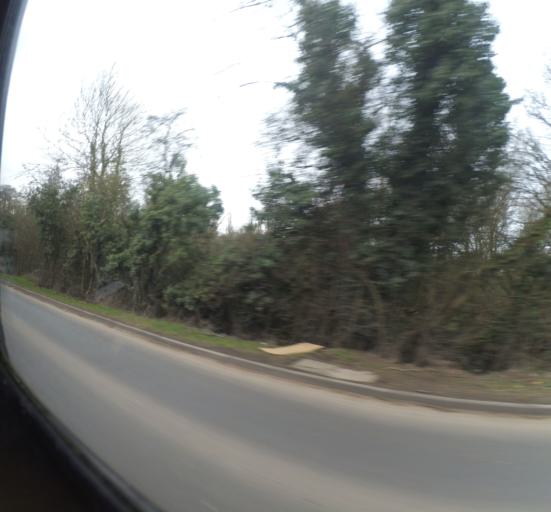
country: GB
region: England
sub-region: Warwickshire
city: Brandon
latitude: 52.4088
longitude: -1.4035
